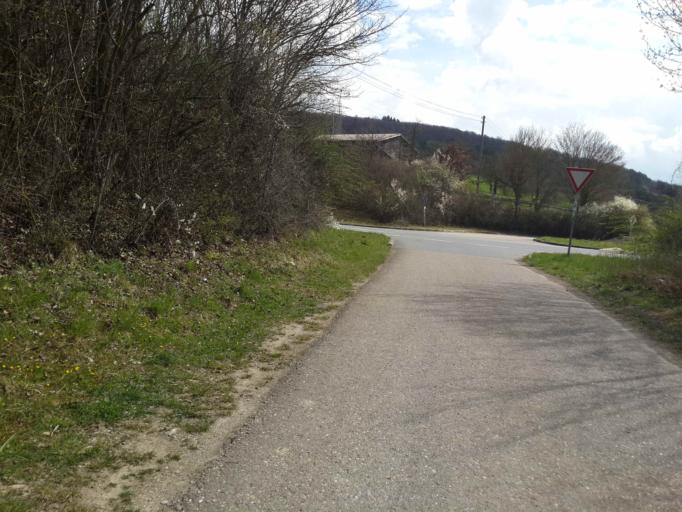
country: DE
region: Baden-Wuerttemberg
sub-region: Regierungsbezirk Stuttgart
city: Bad Mergentheim
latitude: 49.4762
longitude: 9.7725
